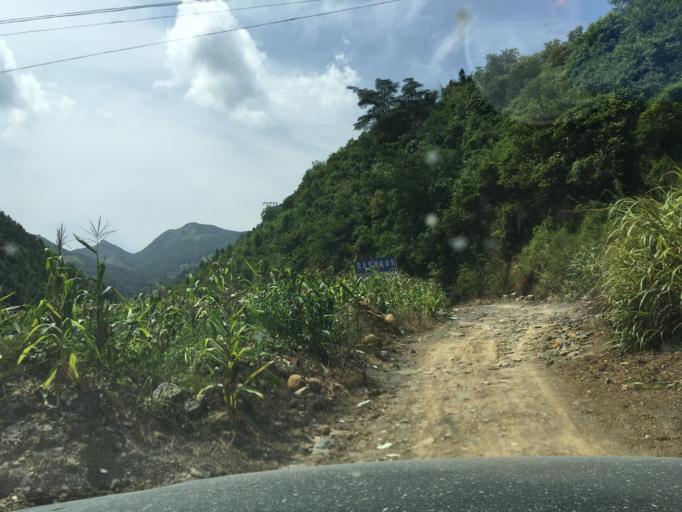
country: CN
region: Guangxi Zhuangzu Zizhiqu
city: Xinzhou
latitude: 24.9534
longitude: 105.7988
